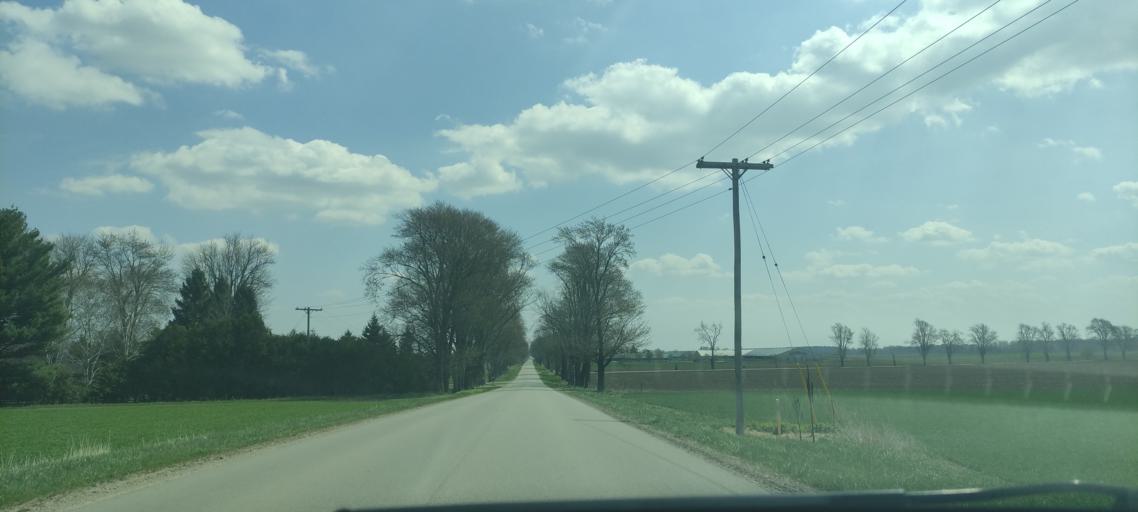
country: CA
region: Ontario
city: Stratford
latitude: 43.3350
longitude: -80.9853
